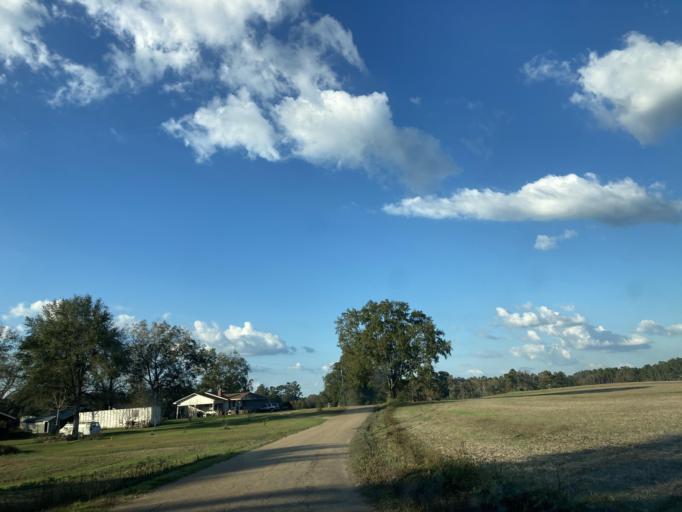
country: US
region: Mississippi
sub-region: Lamar County
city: Sumrall
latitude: 31.3975
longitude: -89.6200
